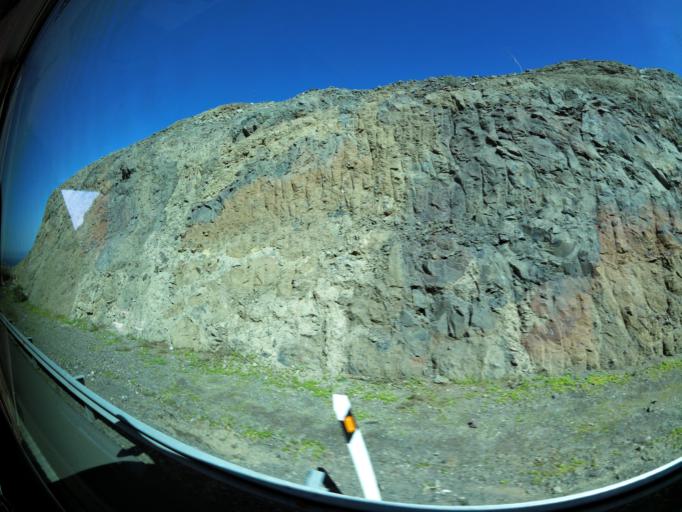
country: ES
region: Canary Islands
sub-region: Provincia de Las Palmas
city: Arucas
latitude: 28.1456
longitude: -15.5168
